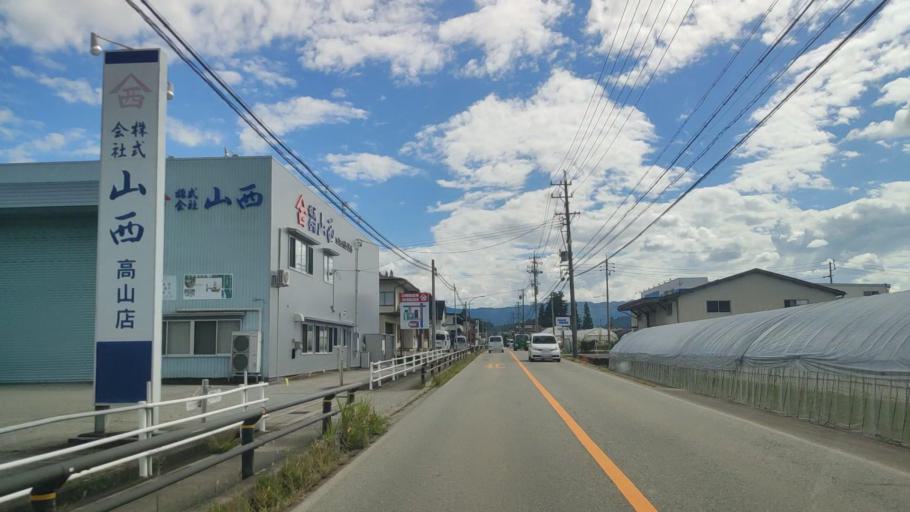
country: JP
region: Gifu
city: Takayama
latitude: 36.1681
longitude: 137.2474
